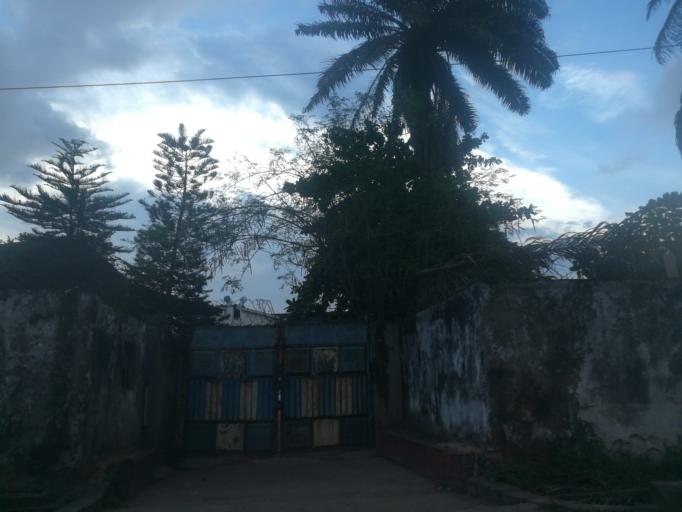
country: NG
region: Lagos
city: Ojota
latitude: 6.5673
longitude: 3.3688
